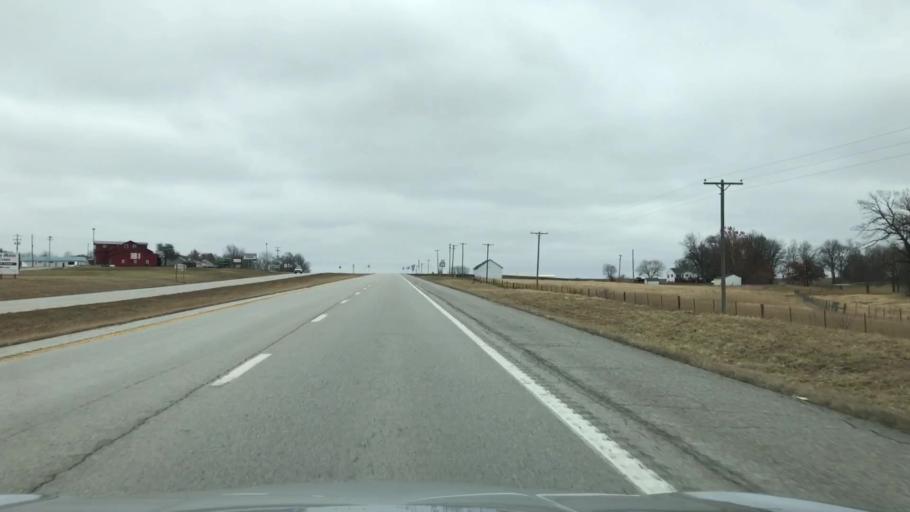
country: US
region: Missouri
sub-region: Livingston County
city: Chillicothe
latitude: 39.7753
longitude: -93.5240
